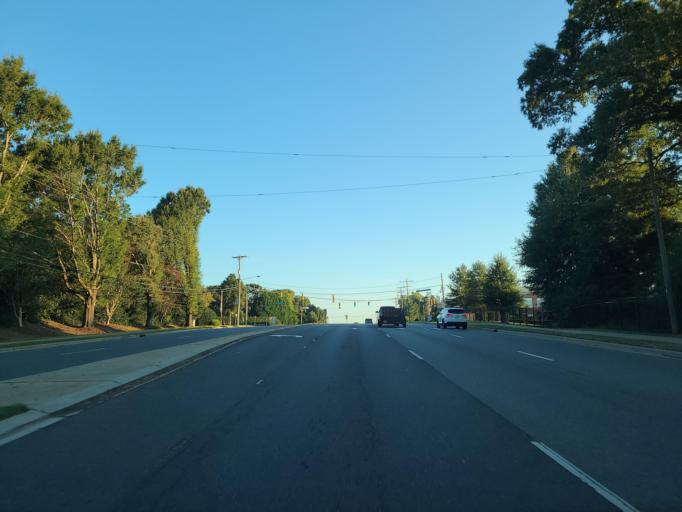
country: US
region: North Carolina
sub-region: Union County
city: Weddington
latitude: 35.0463
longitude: -80.7693
